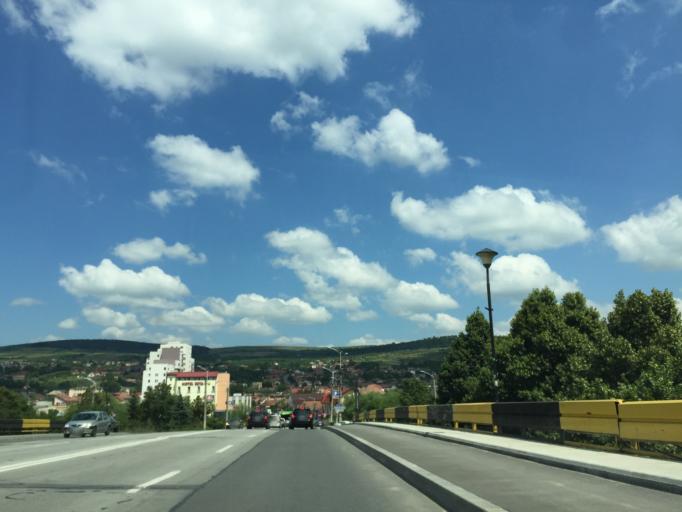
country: RO
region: Cluj
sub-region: Municipiul Cluj-Napoca
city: Cluj-Napoca
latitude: 46.7842
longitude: 23.5823
